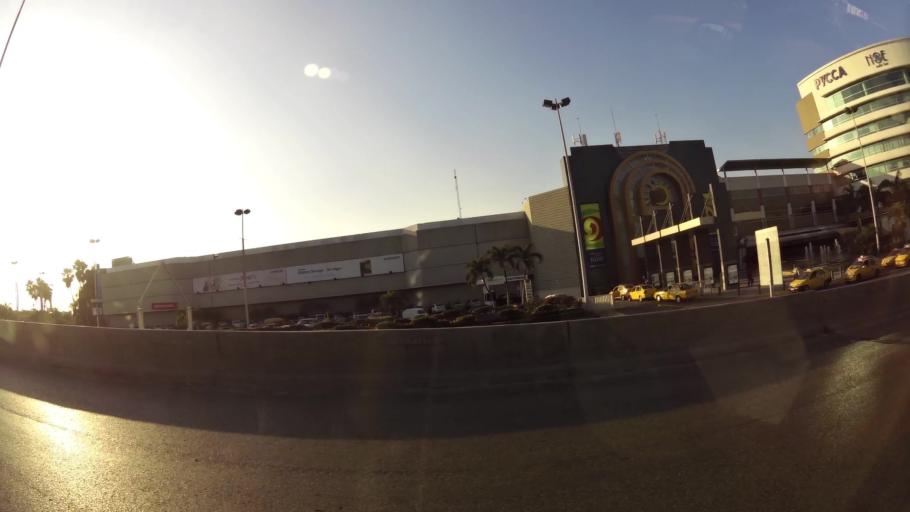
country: EC
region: Guayas
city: Eloy Alfaro
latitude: -2.1562
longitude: -79.8928
